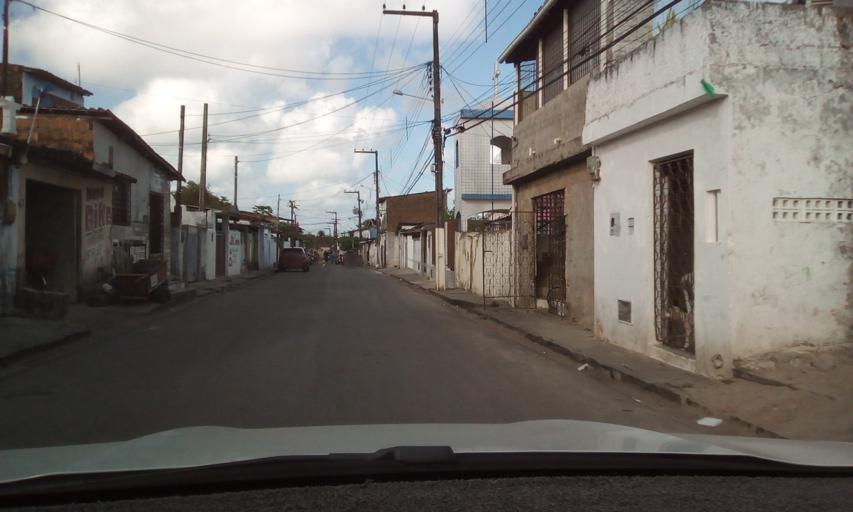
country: BR
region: Paraiba
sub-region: Joao Pessoa
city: Joao Pessoa
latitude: -7.0979
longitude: -34.8620
